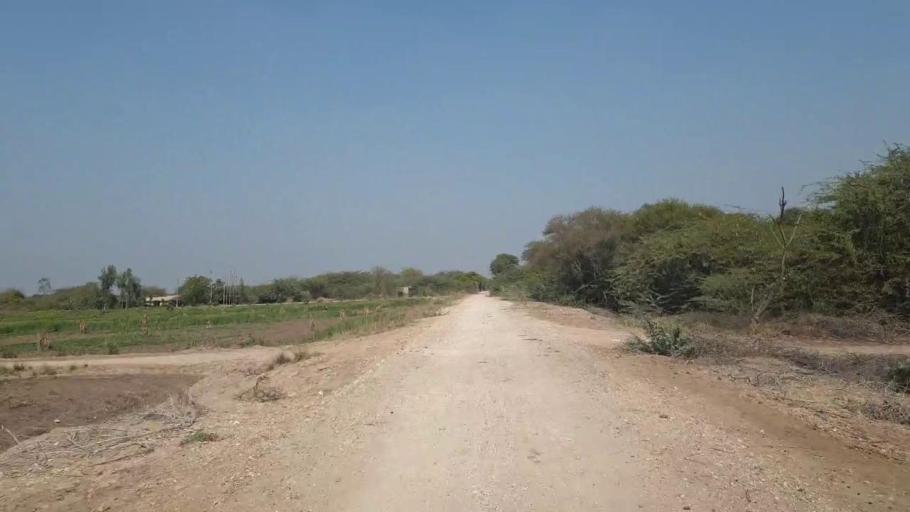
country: PK
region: Sindh
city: Chambar
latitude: 25.4026
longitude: 68.9018
